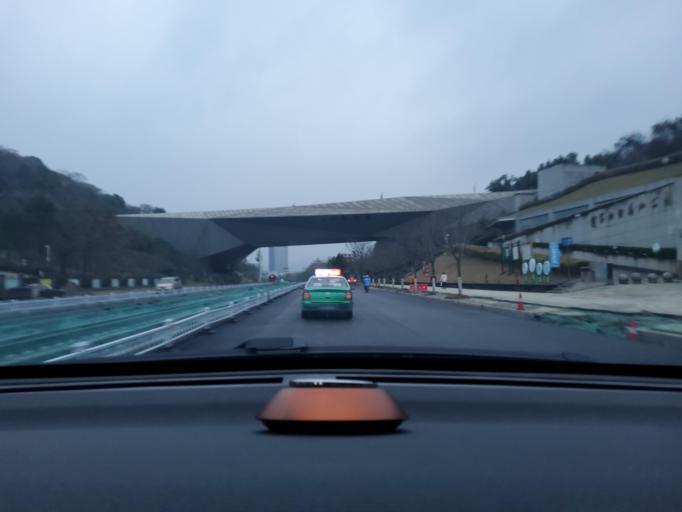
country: CN
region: Hubei
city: Tuanchengshan
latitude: 30.1944
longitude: 115.0219
